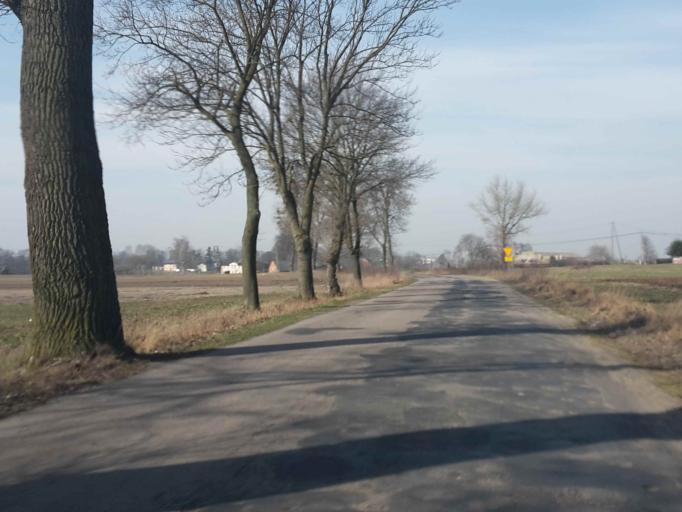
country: PL
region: Kujawsko-Pomorskie
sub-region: Powiat wabrzeski
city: Debowa Laka
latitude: 53.2143
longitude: 19.1879
